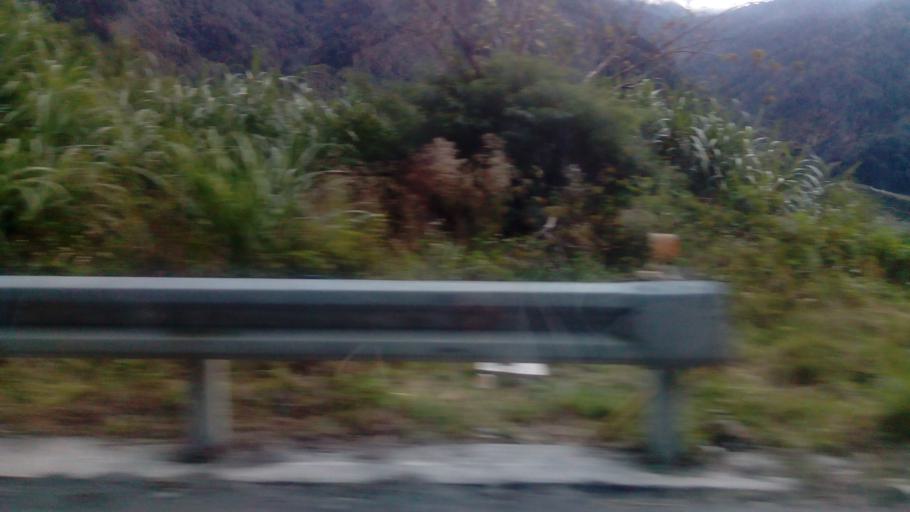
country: TW
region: Taiwan
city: Daxi
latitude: 24.4522
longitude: 121.3902
